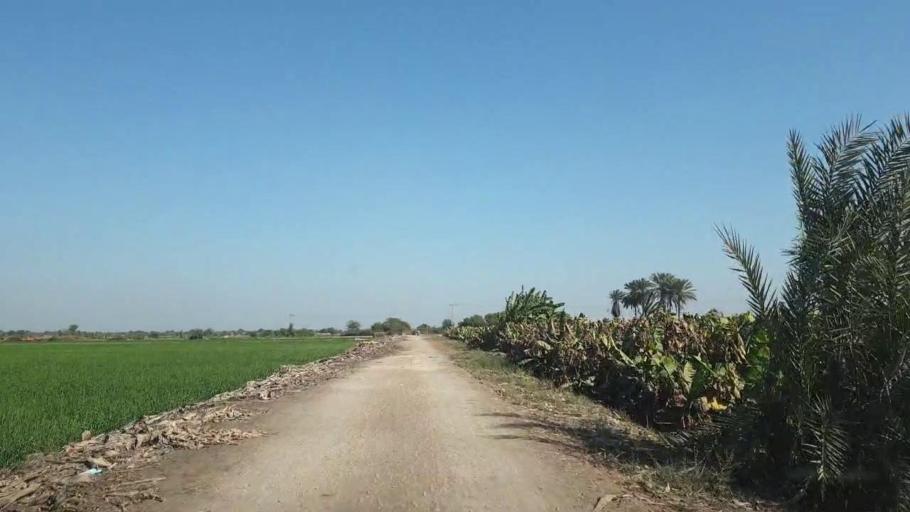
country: PK
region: Sindh
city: Tando Adam
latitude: 25.6624
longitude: 68.6903
